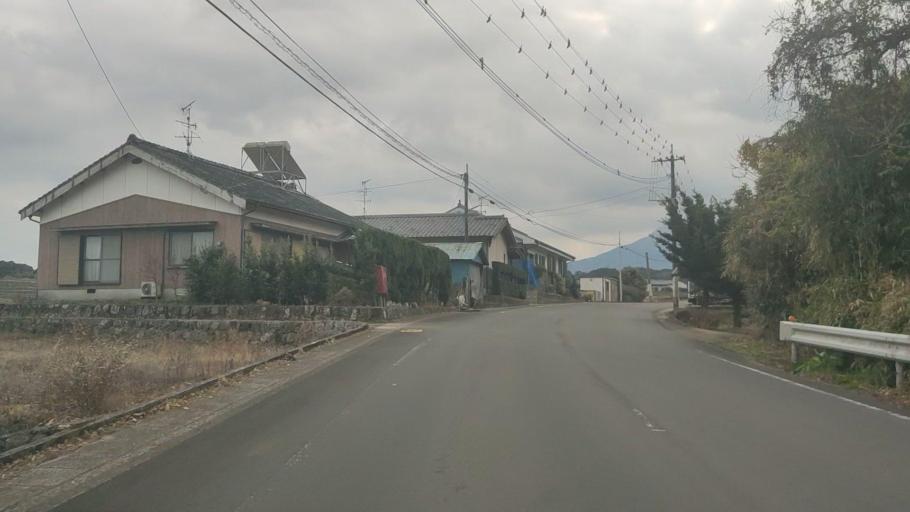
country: JP
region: Nagasaki
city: Shimabara
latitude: 32.8332
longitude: 130.2915
